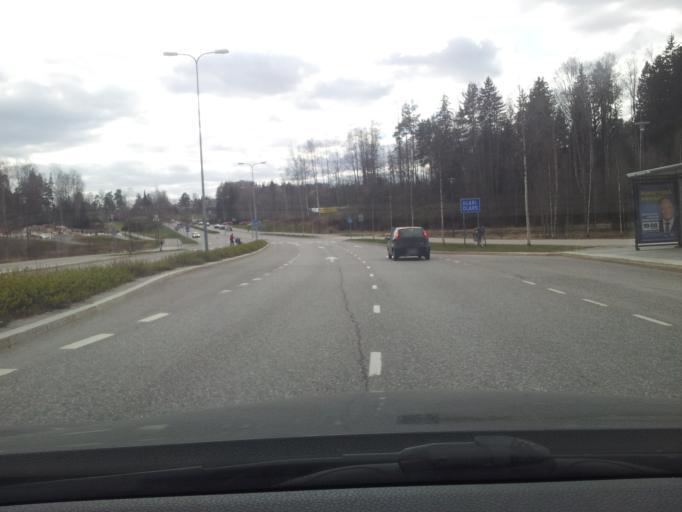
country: FI
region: Uusimaa
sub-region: Helsinki
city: Koukkuniemi
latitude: 60.1811
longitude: 24.7442
